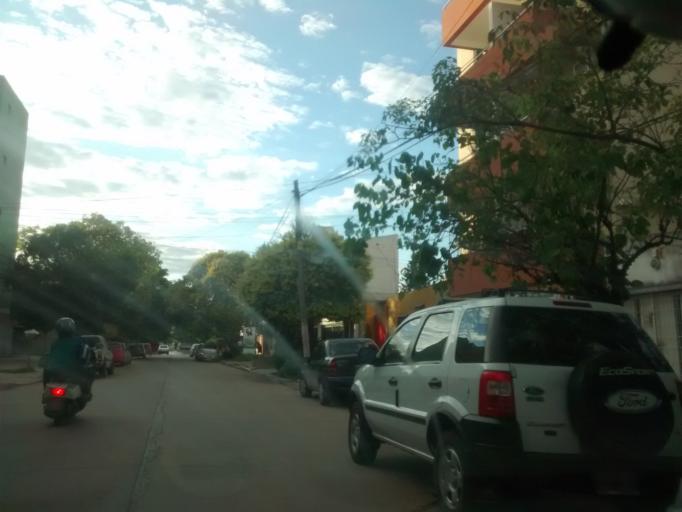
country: AR
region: Chaco
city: Resistencia
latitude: -27.4608
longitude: -58.9809
